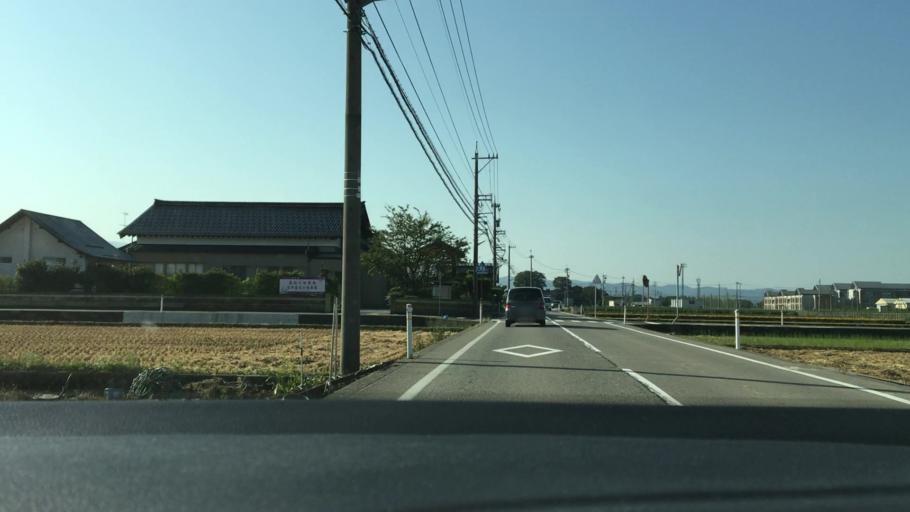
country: JP
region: Ishikawa
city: Nonoichi
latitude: 36.5118
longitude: 136.5997
